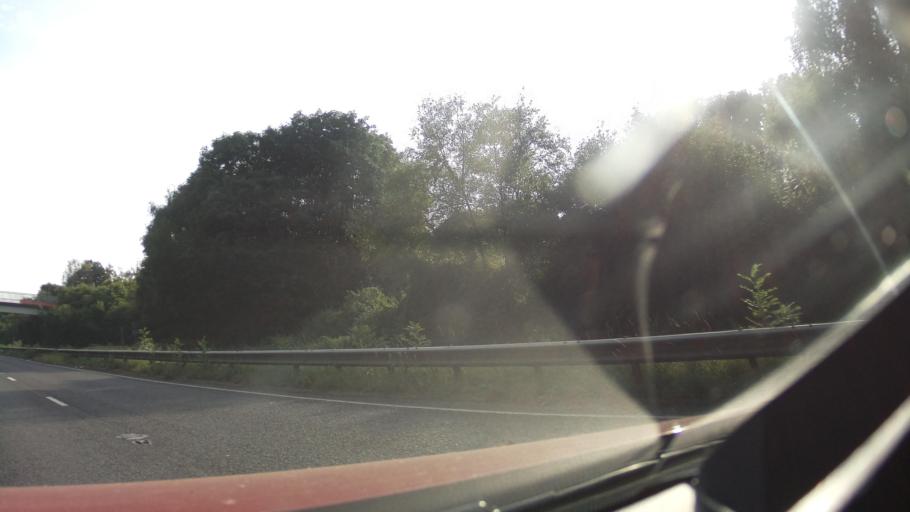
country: GB
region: England
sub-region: Warwickshire
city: Alcester
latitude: 52.2189
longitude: -1.8832
